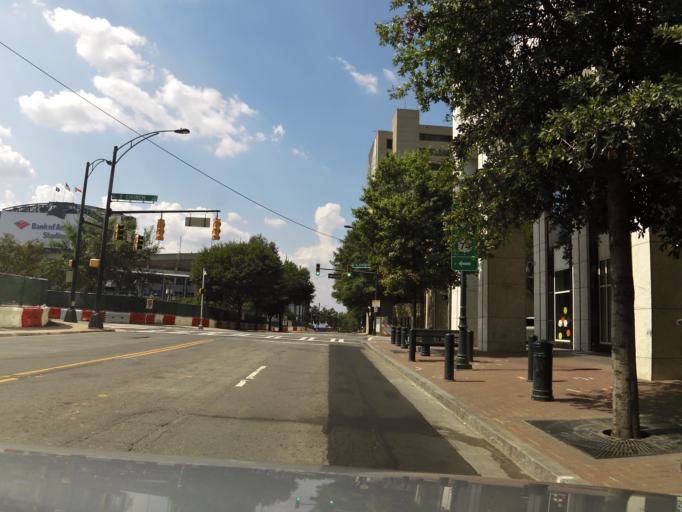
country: US
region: North Carolina
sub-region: Mecklenburg County
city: Charlotte
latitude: 35.2242
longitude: -80.8491
